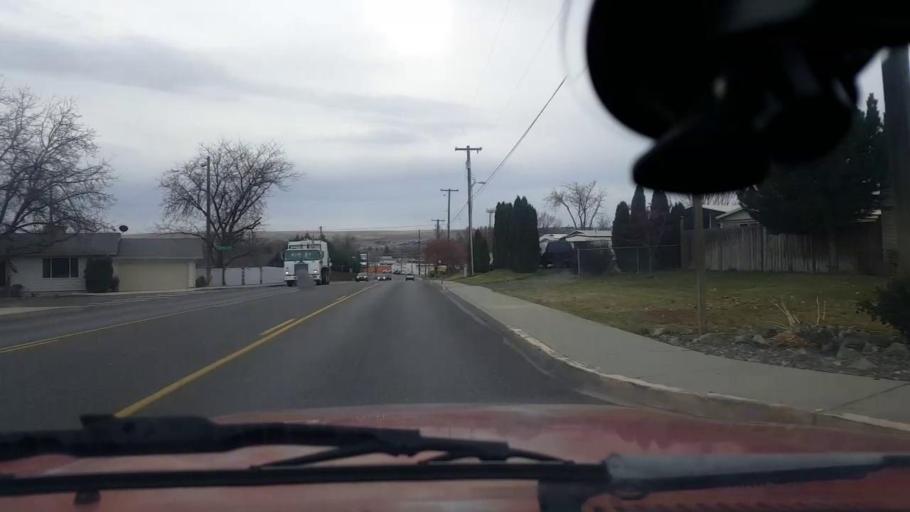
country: US
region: Washington
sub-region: Asotin County
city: Clarkston Heights-Vineland
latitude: 46.3989
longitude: -117.0814
